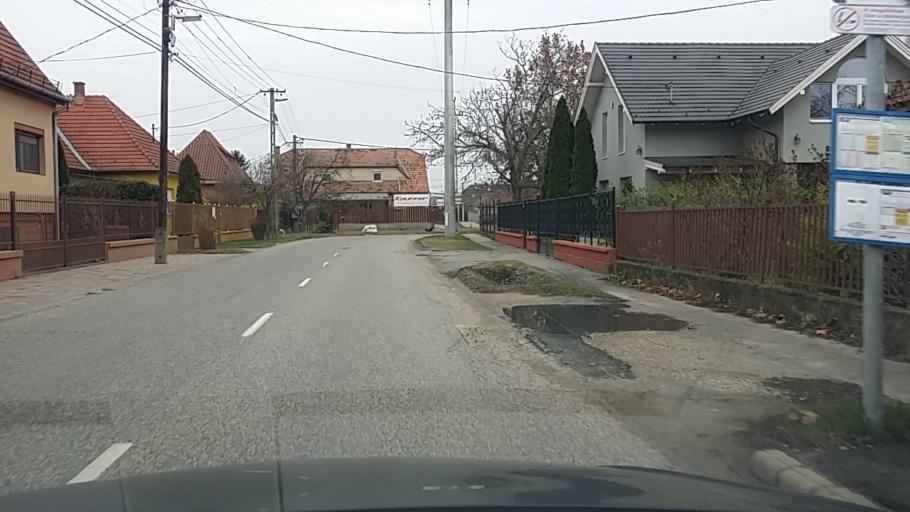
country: HU
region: Pest
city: Szigetszentmiklos
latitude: 47.3551
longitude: 19.0258
